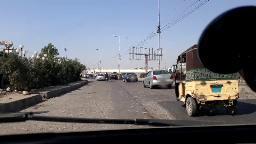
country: PK
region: Sindh
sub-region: Karachi District
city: Karachi
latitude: 24.9012
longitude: 67.1120
